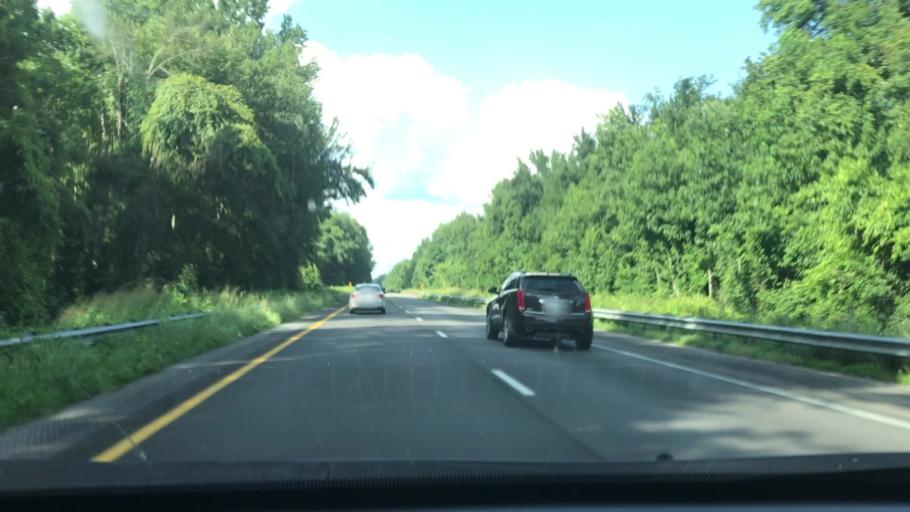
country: US
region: South Carolina
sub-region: Clarendon County
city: Manning
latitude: 33.8319
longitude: -80.1319
